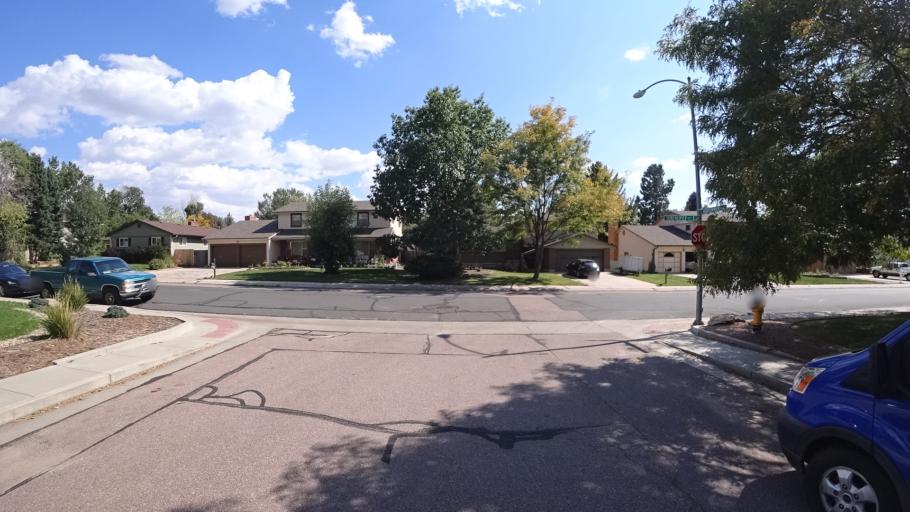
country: US
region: Colorado
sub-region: El Paso County
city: Cimarron Hills
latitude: 38.8713
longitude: -104.7527
